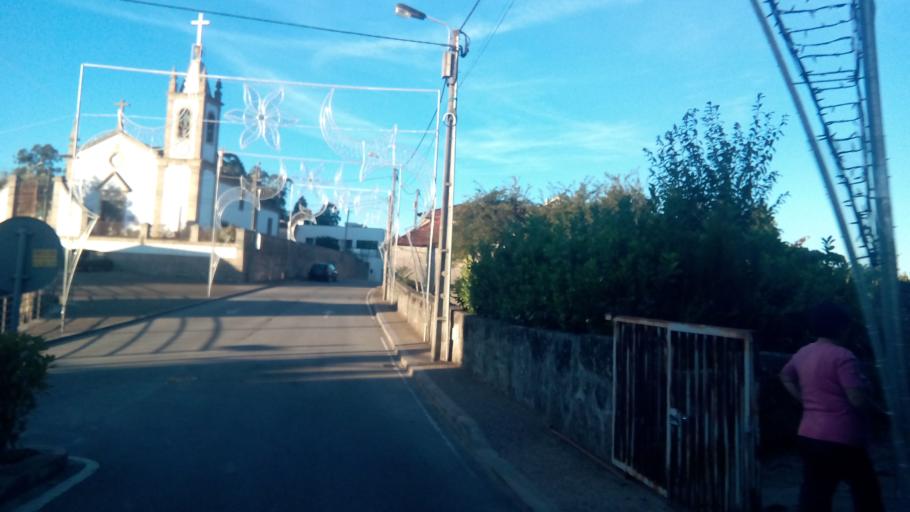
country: PT
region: Porto
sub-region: Paredes
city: Baltar
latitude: 41.1841
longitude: -8.3769
